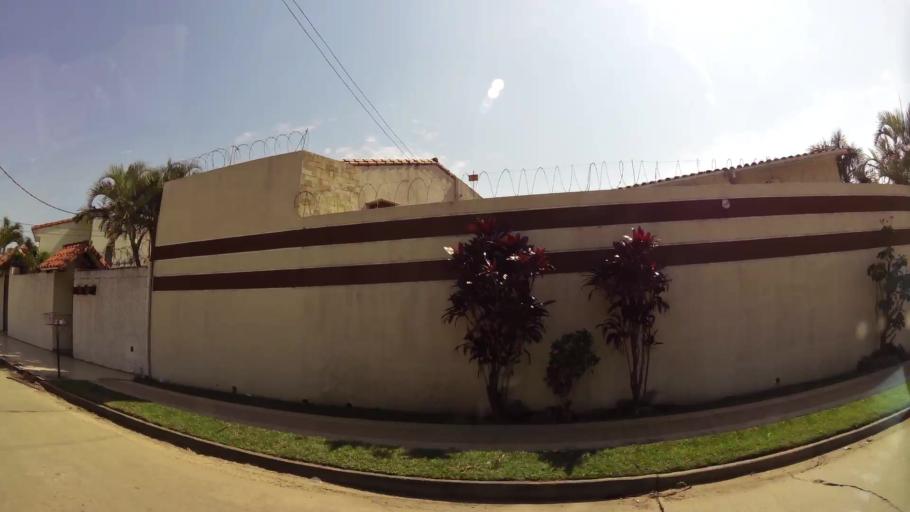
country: BO
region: Santa Cruz
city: Santa Cruz de la Sierra
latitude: -17.7444
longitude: -63.1695
